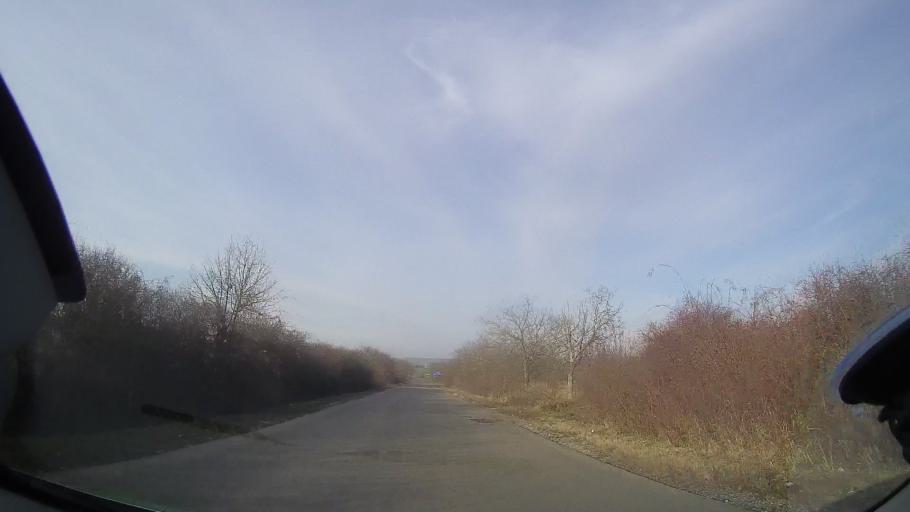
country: RO
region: Bihor
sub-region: Comuna Spinus
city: Spinus
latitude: 47.2247
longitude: 22.1687
